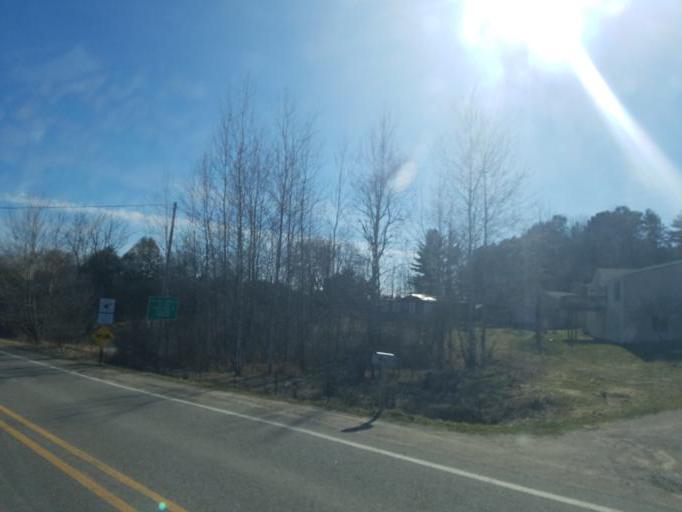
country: US
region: Michigan
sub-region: Isabella County
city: Lake Isabella
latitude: 43.5525
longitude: -85.0857
